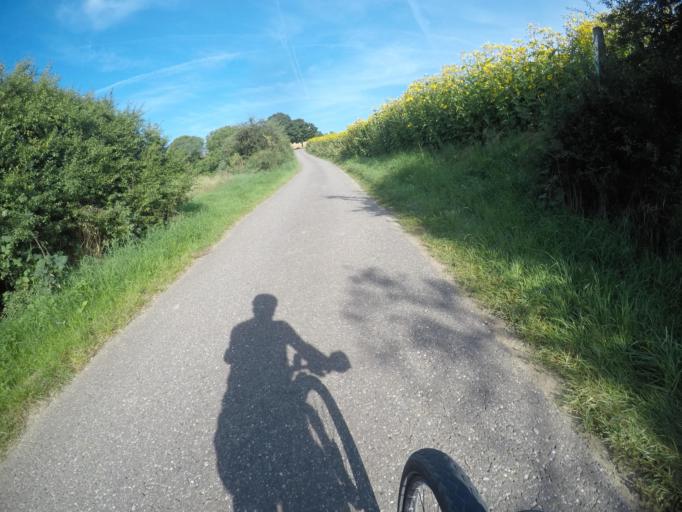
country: DE
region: Baden-Wuerttemberg
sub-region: Regierungsbezirk Stuttgart
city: Weissach
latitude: 48.8544
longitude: 8.9362
